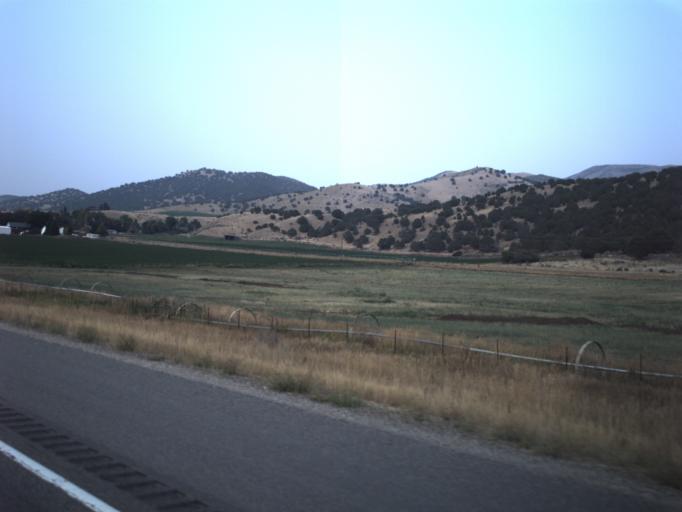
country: US
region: Utah
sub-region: Summit County
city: Coalville
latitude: 40.8416
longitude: -111.3872
